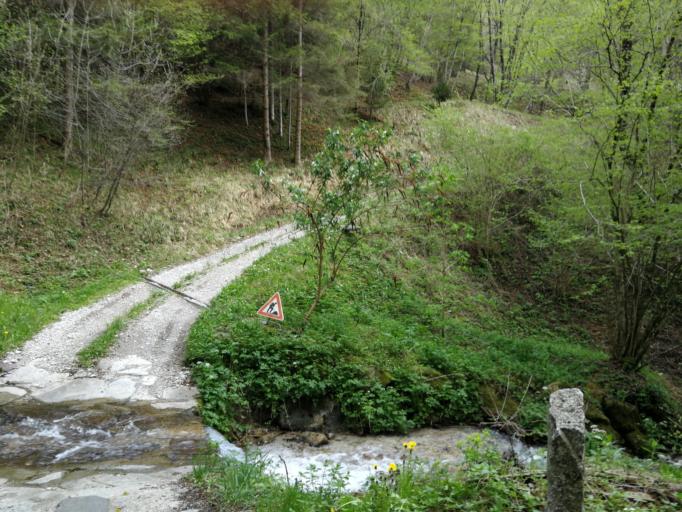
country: IT
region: Trentino-Alto Adige
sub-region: Provincia di Trento
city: Creto
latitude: 45.9330
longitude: 10.6444
